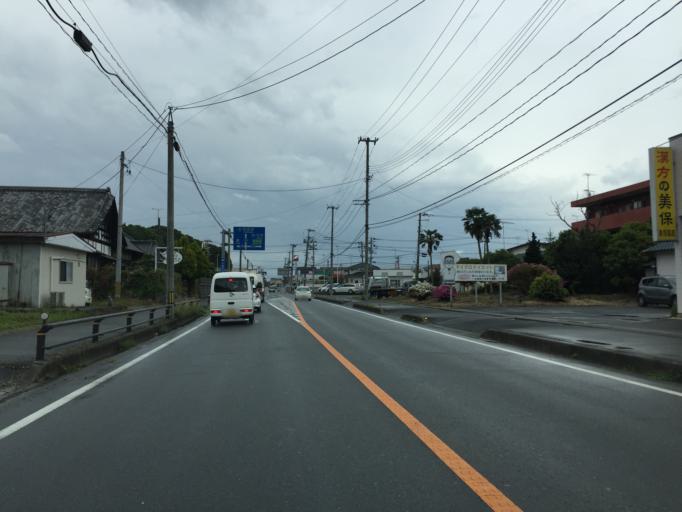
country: JP
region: Ibaraki
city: Kitaibaraki
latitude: 36.9234
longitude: 140.7845
